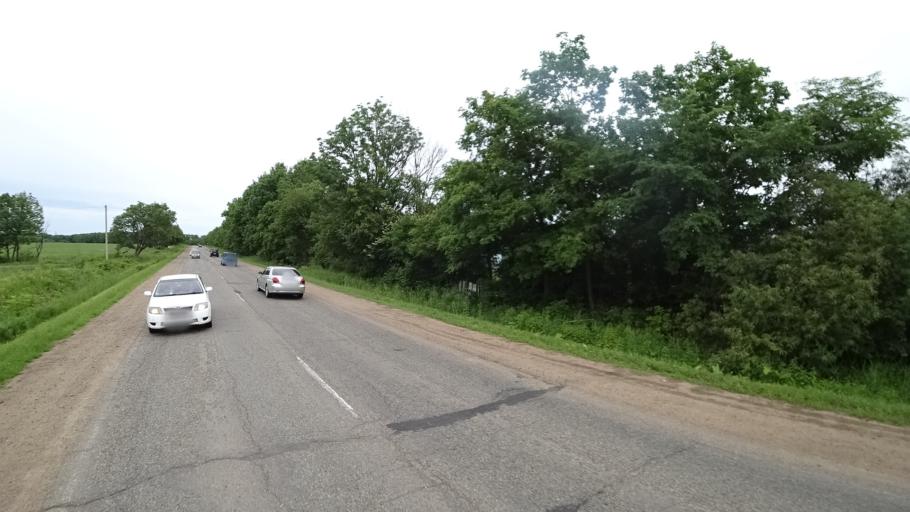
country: RU
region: Primorskiy
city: Novosysoyevka
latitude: 44.1836
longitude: 133.3514
